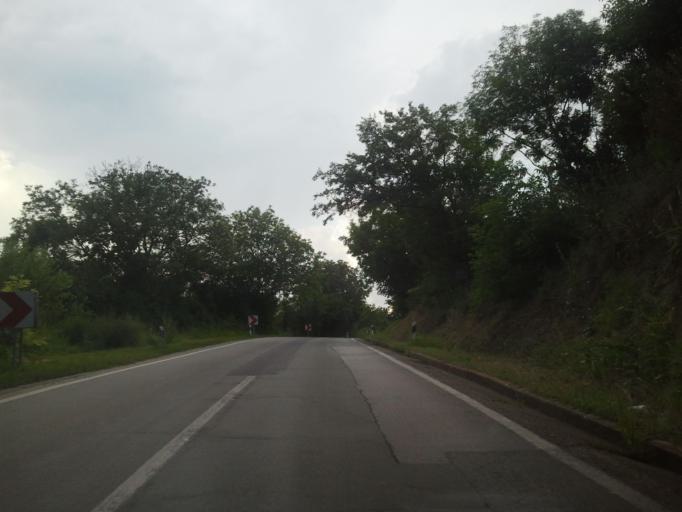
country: HR
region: Vukovarsko-Srijemska
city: Lovas
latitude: 45.2502
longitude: 19.2124
